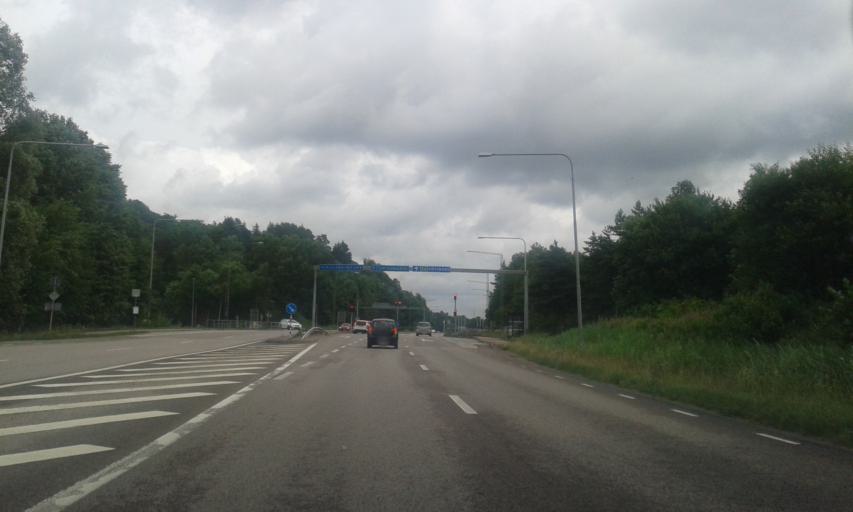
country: SE
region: Vaestra Goetaland
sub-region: Kungalvs Kommun
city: Kungalv
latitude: 57.8700
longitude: 11.9427
